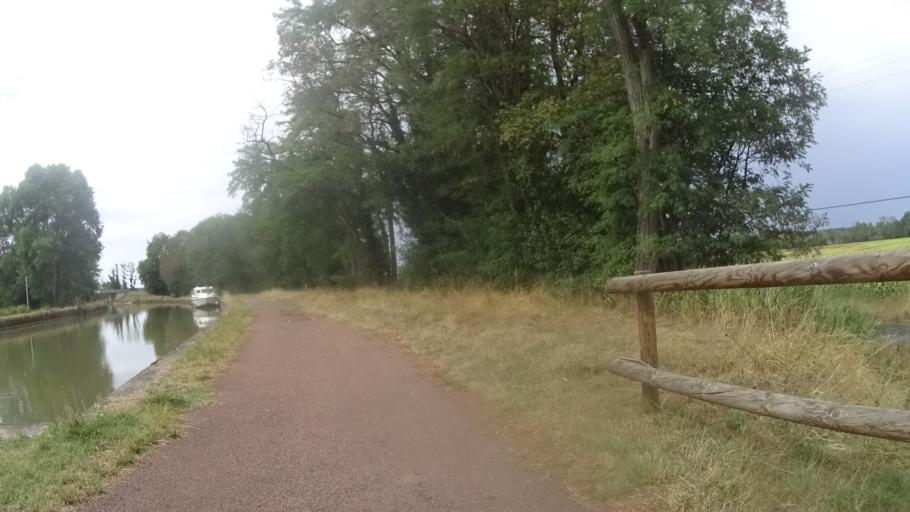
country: FR
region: Bourgogne
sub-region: Departement de la Nievre
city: Imphy
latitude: 46.9244
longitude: 3.2373
